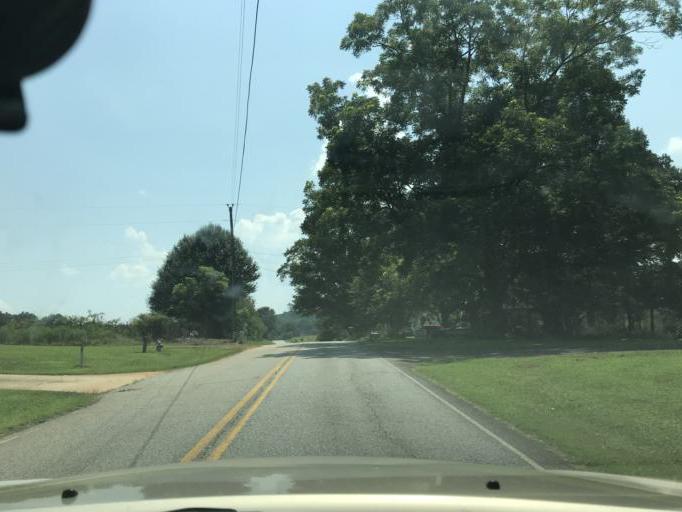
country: US
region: Georgia
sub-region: Dawson County
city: Dawsonville
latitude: 34.3229
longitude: -84.0997
